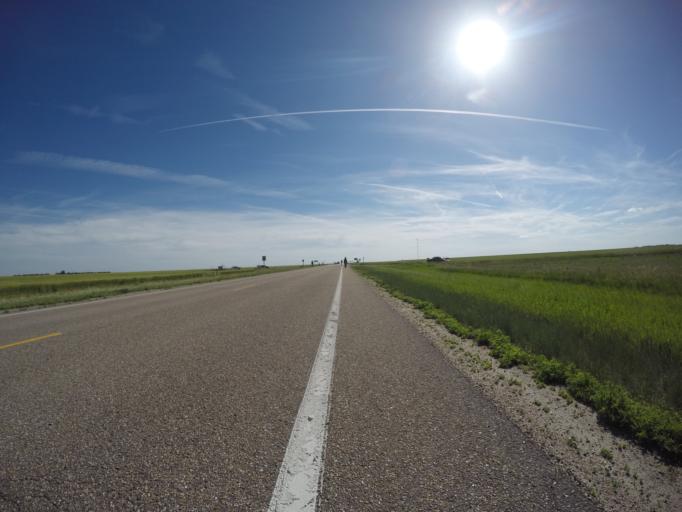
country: US
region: Kansas
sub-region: Cheyenne County
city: Saint Francis
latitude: 39.7520
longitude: -102.0491
